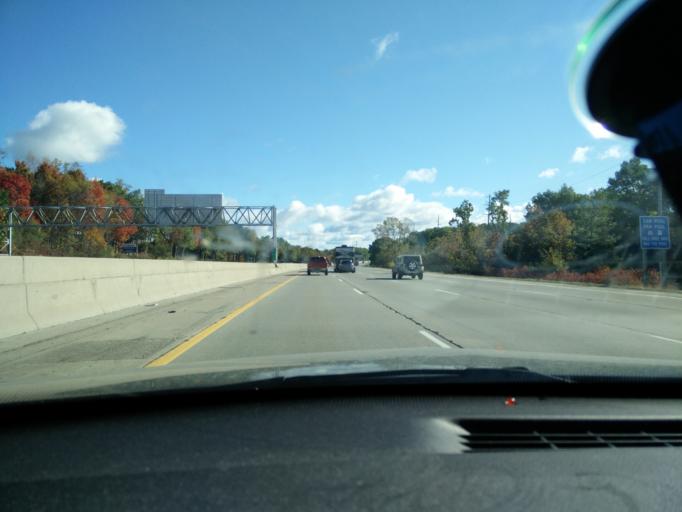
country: US
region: Michigan
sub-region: Oakland County
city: Farmington Hills
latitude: 42.4924
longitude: -83.4133
